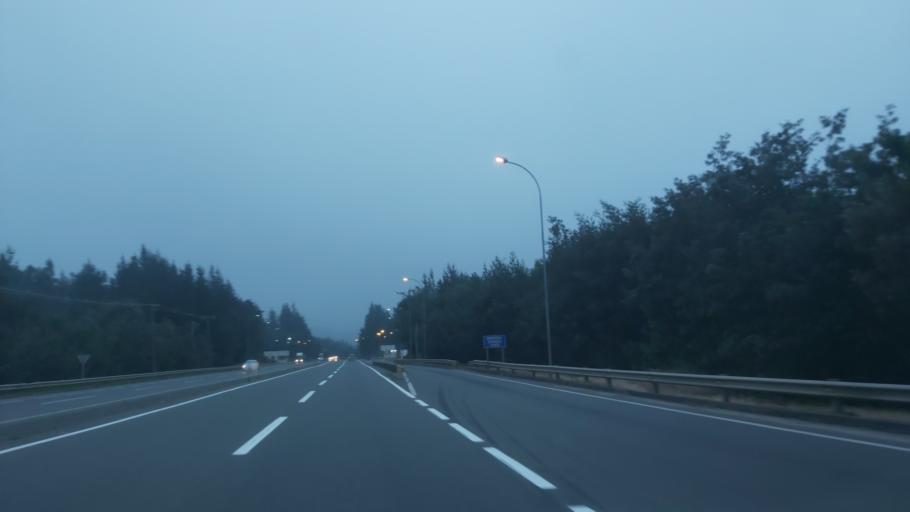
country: CL
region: Biobio
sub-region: Provincia de Concepcion
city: Penco
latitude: -36.7343
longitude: -72.8858
